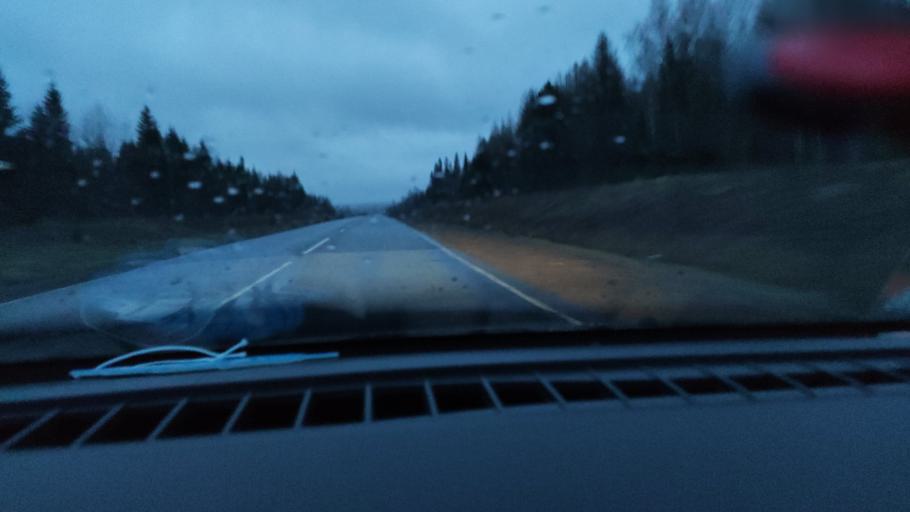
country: RU
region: Udmurtiya
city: Mozhga
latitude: 56.3327
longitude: 52.3034
